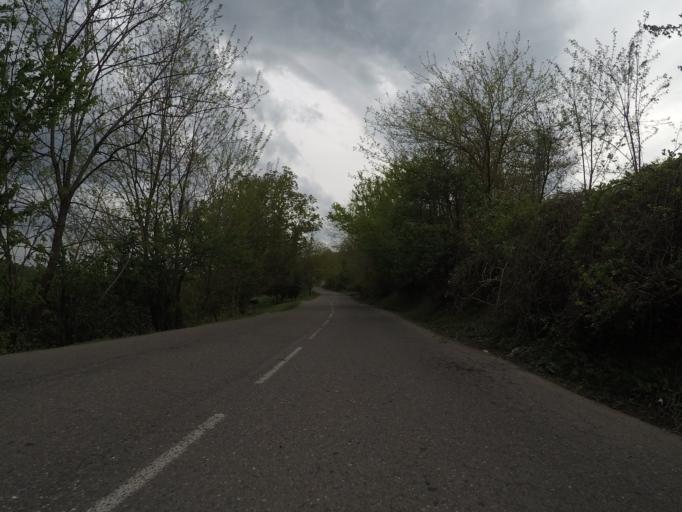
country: GE
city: Tqibuli
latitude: 42.2826
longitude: 43.2068
